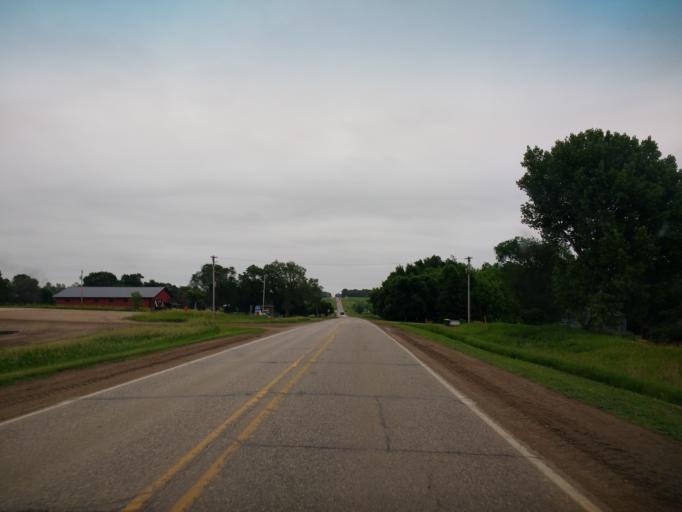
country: US
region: Iowa
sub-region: Dickinson County
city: Milford
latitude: 43.3278
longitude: -95.1397
